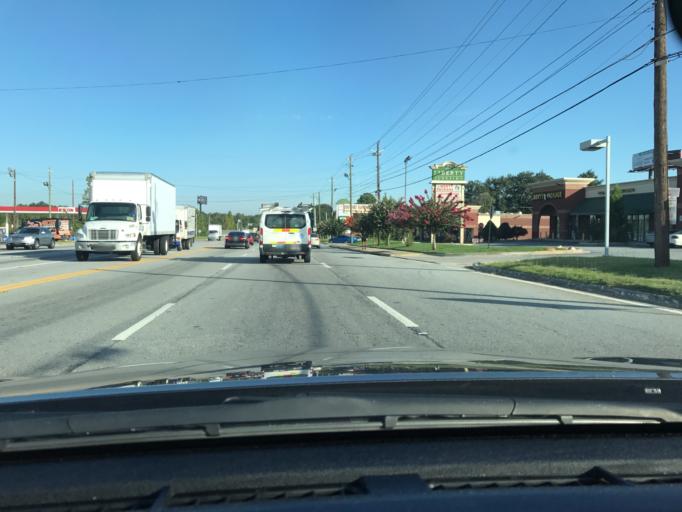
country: US
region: Georgia
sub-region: Clayton County
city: Forest Park
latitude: 33.6298
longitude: -84.3856
